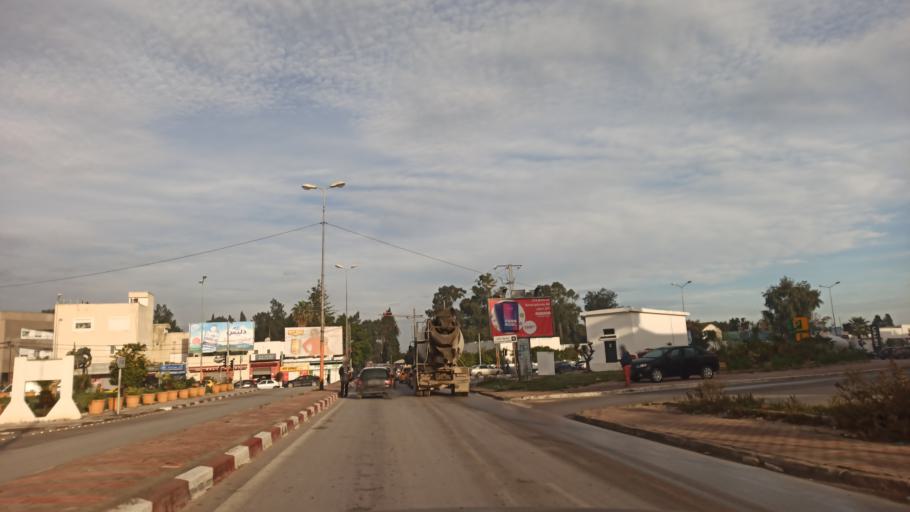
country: TN
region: Ariana
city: Ariana
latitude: 36.8747
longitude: 10.2460
